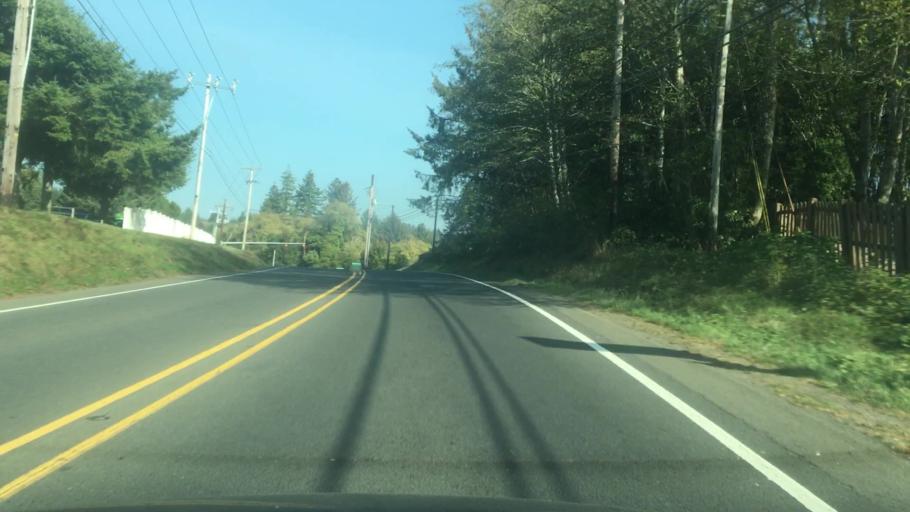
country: US
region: Oregon
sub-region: Lincoln County
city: Lincoln City
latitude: 45.0007
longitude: -123.9882
